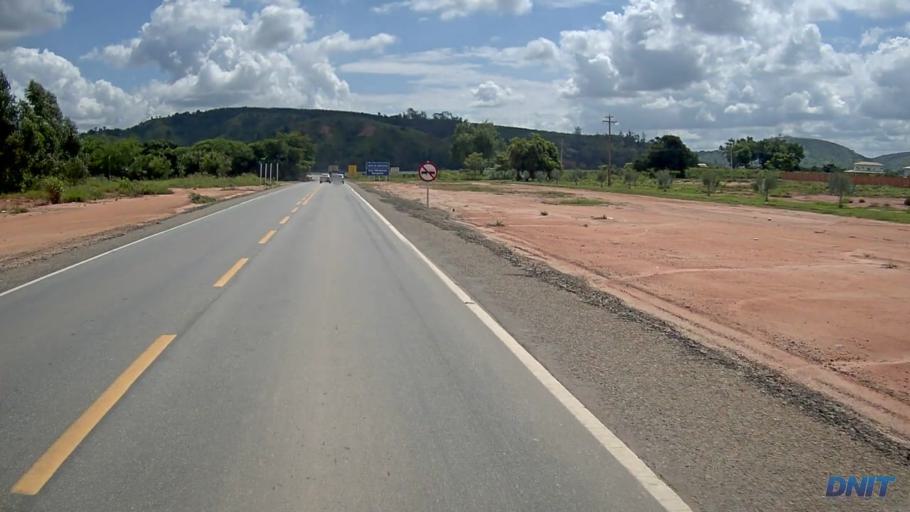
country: BR
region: Minas Gerais
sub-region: Governador Valadares
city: Governador Valadares
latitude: -19.0446
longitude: -42.1521
